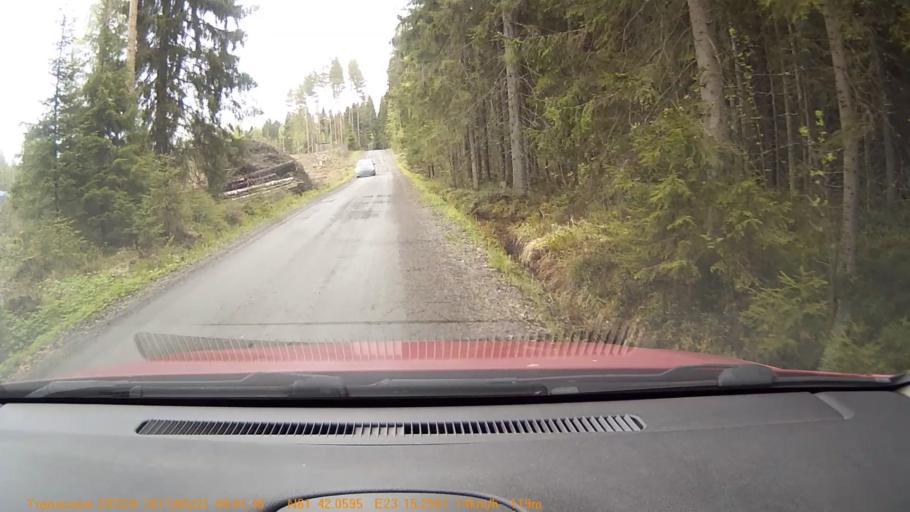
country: FI
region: Pirkanmaa
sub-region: Tampere
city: Viljakkala
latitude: 61.7010
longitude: 23.2541
